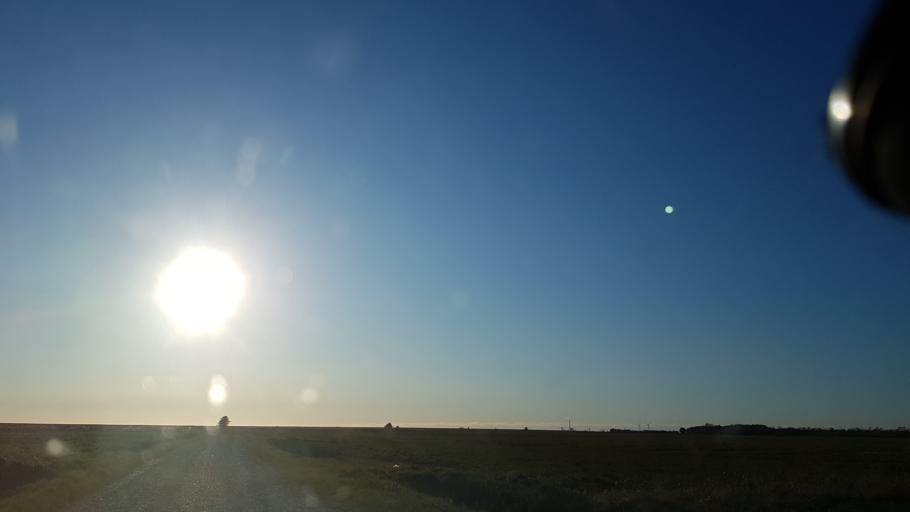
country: DK
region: South Denmark
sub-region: Esbjerg Kommune
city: Bramming
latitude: 55.4085
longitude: 8.6743
